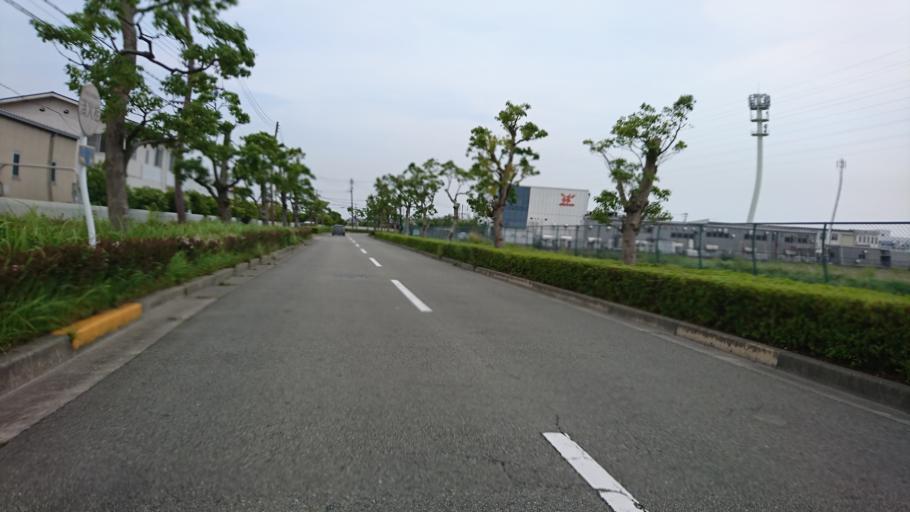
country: JP
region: Hyogo
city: Kakogawacho-honmachi
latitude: 34.7394
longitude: 134.8845
